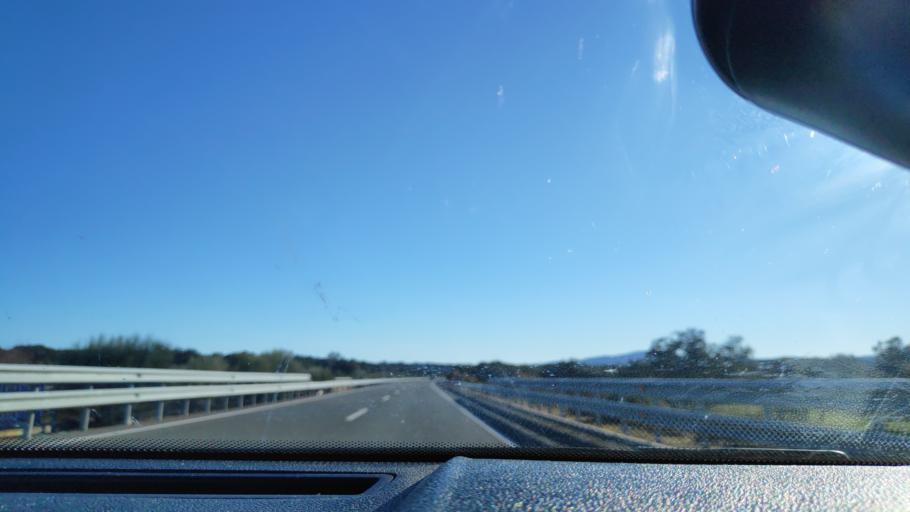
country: ES
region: Andalusia
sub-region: Provincia de Huelva
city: Cala
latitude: 37.9908
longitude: -6.2330
